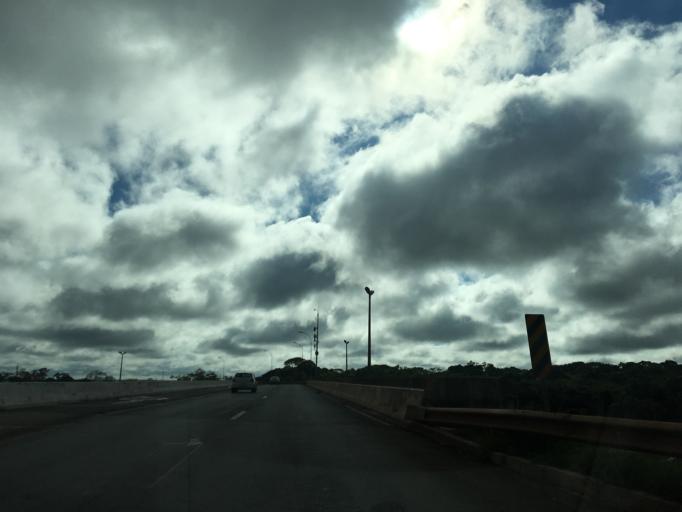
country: BR
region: Federal District
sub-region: Brasilia
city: Brasilia
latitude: -15.9475
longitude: -47.9930
